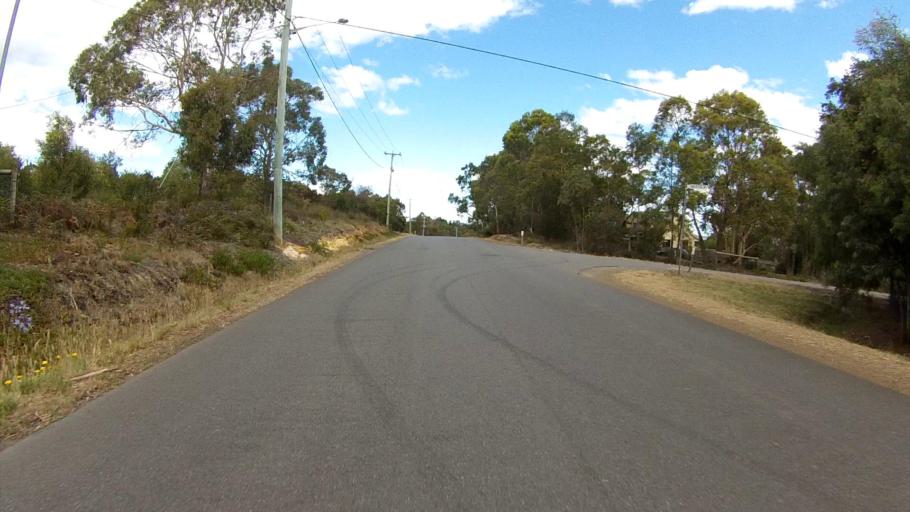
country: AU
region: Tasmania
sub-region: Clarence
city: Acton Park
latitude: -42.8753
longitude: 147.4896
